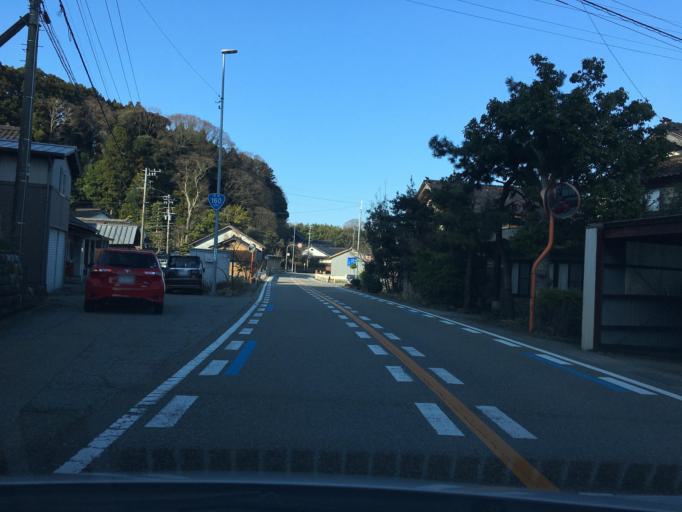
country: JP
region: Toyama
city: Himi
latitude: 36.9503
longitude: 137.0389
